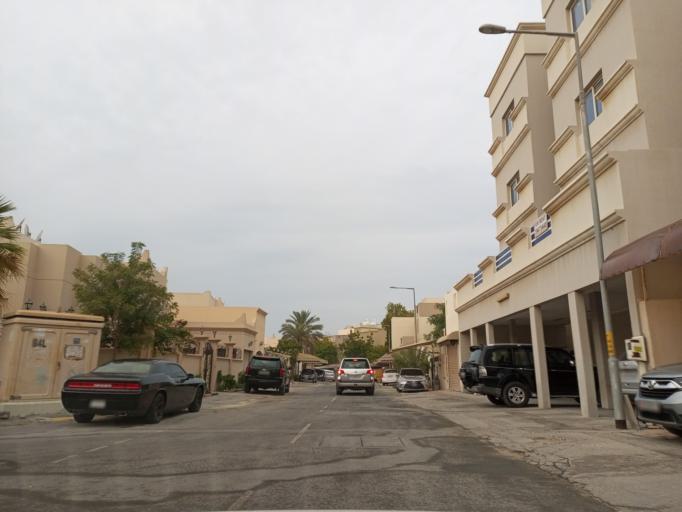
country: BH
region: Muharraq
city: Al Hadd
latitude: 26.2452
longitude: 50.6438
